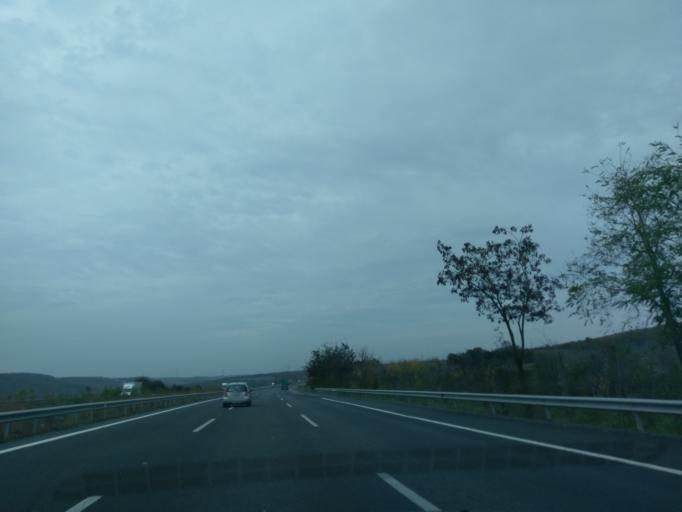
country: TR
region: Istanbul
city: Canta
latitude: 41.1698
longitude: 28.1219
